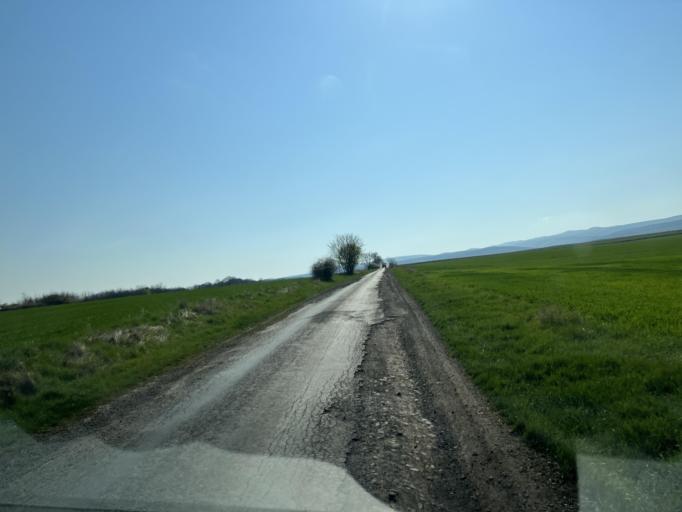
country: SK
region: Nitriansky
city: Sahy
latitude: 48.0481
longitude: 18.8690
